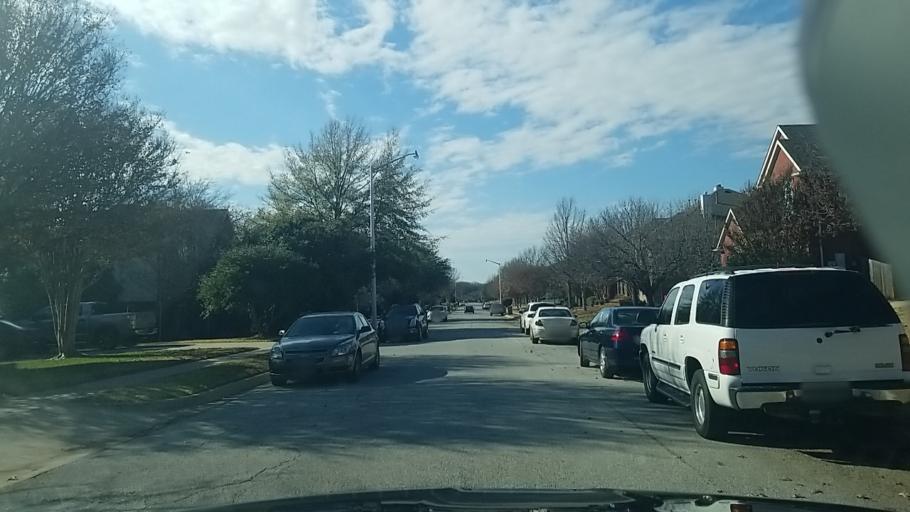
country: US
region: Texas
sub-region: Denton County
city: Corinth
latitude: 33.1478
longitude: -97.1170
